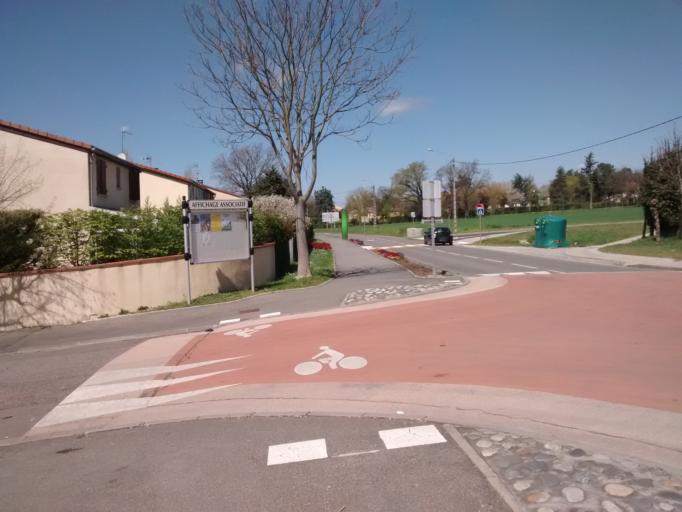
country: FR
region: Midi-Pyrenees
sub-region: Departement de la Haute-Garonne
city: Labege
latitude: 43.5308
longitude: 1.5257
